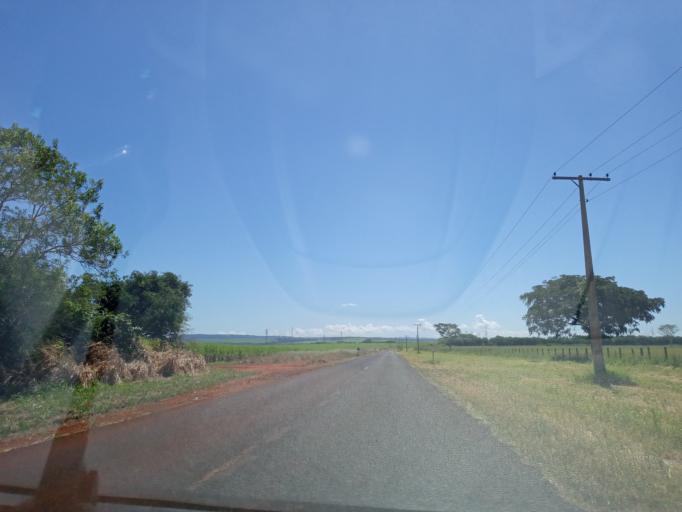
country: BR
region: Goias
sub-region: Itumbiara
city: Itumbiara
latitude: -18.4096
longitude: -49.1269
